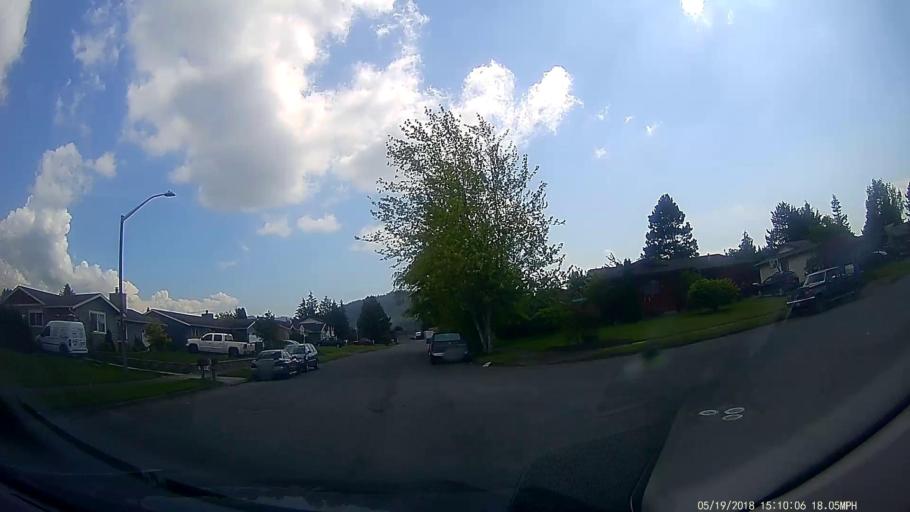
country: US
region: Washington
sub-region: Skagit County
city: Mount Vernon
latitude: 48.4188
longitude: -122.3085
